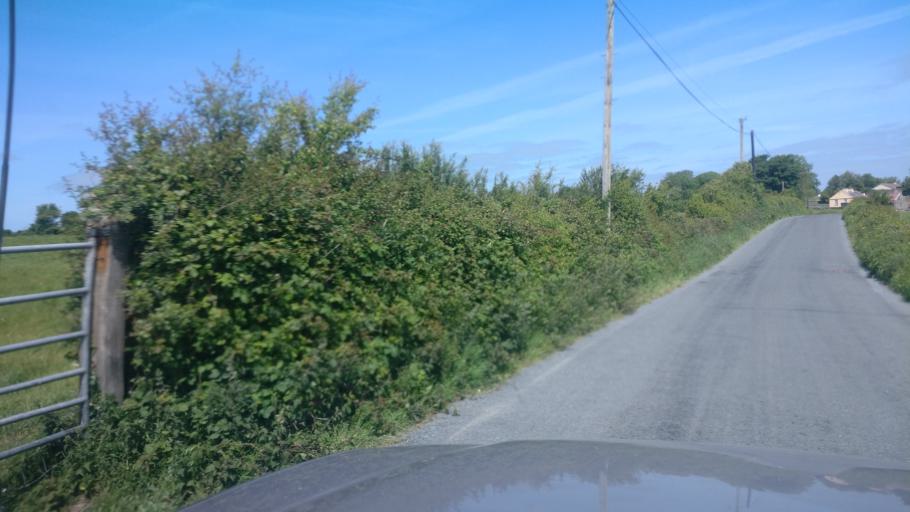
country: IE
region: Connaught
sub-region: County Galway
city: Gort
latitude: 53.0772
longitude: -8.8026
